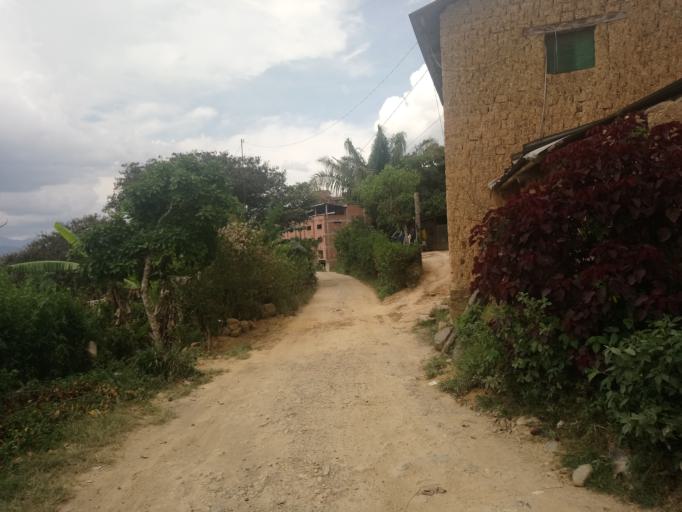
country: BO
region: La Paz
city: Coroico
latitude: -16.1889
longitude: -67.7298
